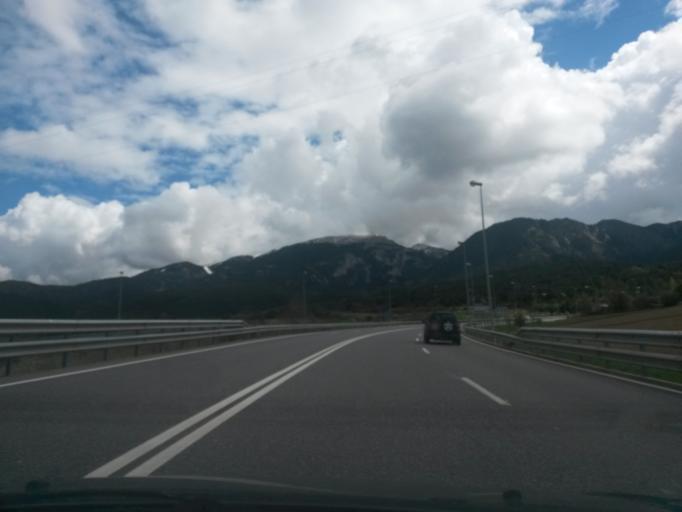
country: ES
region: Catalonia
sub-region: Provincia de Lleida
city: Riu de Cerdanya
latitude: 42.3489
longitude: 1.8313
